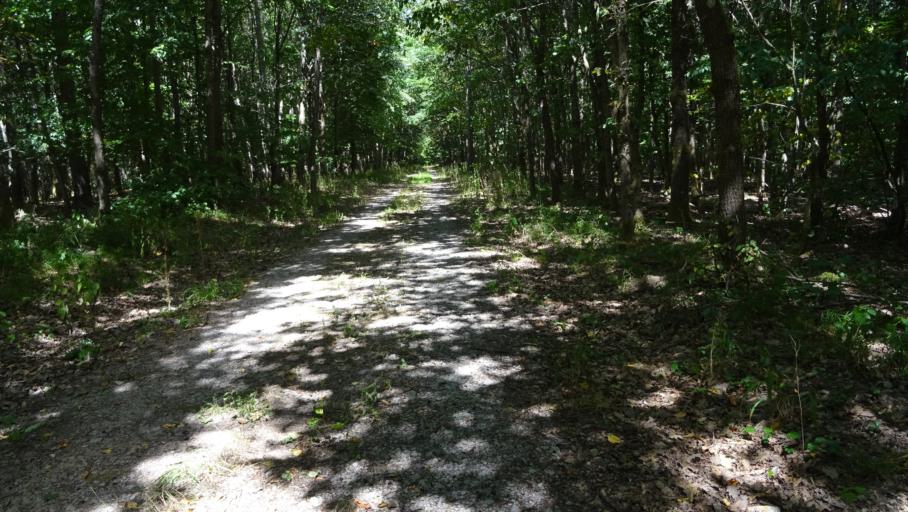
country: DE
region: Baden-Wuerttemberg
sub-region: Karlsruhe Region
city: Neckargerach
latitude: 49.3811
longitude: 9.0858
